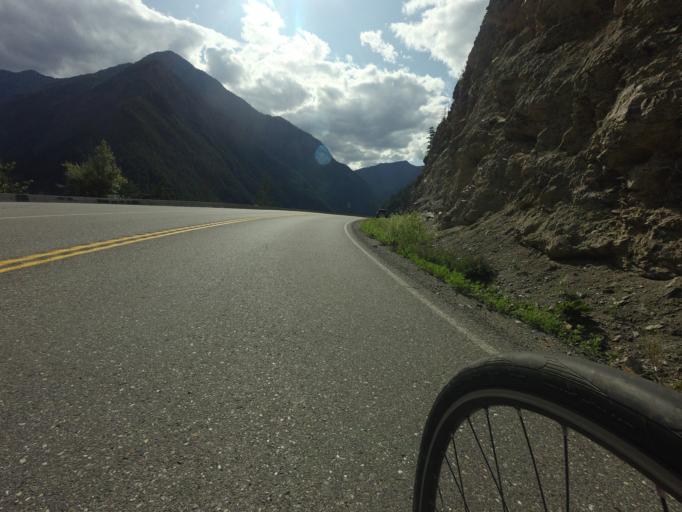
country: CA
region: British Columbia
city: Lillooet
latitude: 50.6418
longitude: -122.0259
